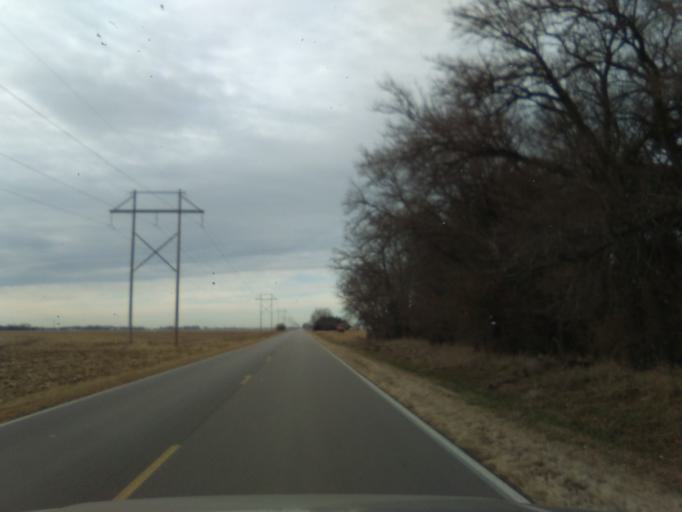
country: US
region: Nebraska
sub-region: Buffalo County
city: Gibbon
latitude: 40.6549
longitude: -98.8147
